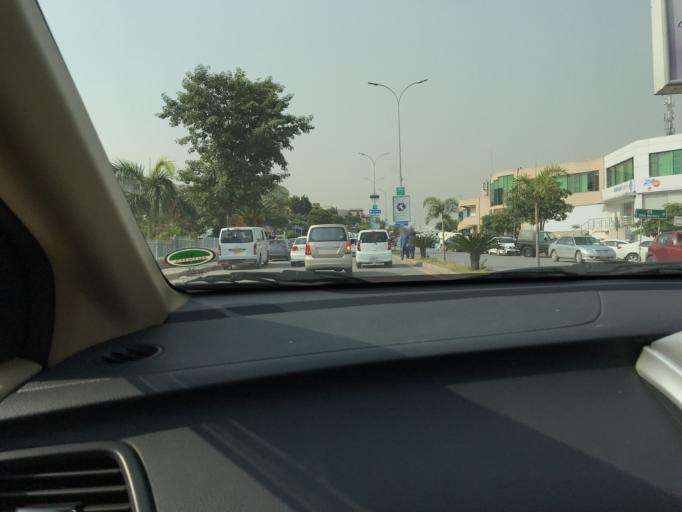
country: PK
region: Punjab
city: Rawalpindi
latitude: 33.5388
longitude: 73.0994
